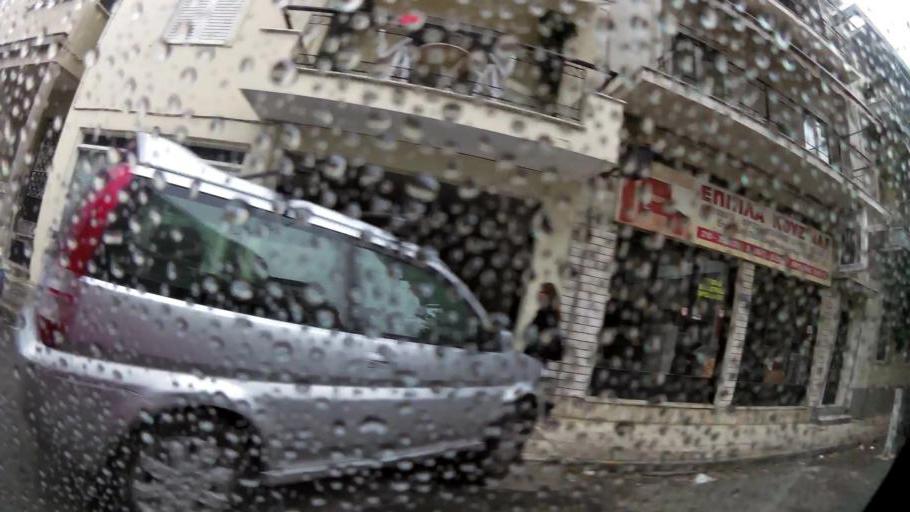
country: GR
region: Attica
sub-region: Nomarchia Athinas
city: Agioi Anargyroi
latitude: 38.0252
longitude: 23.7214
